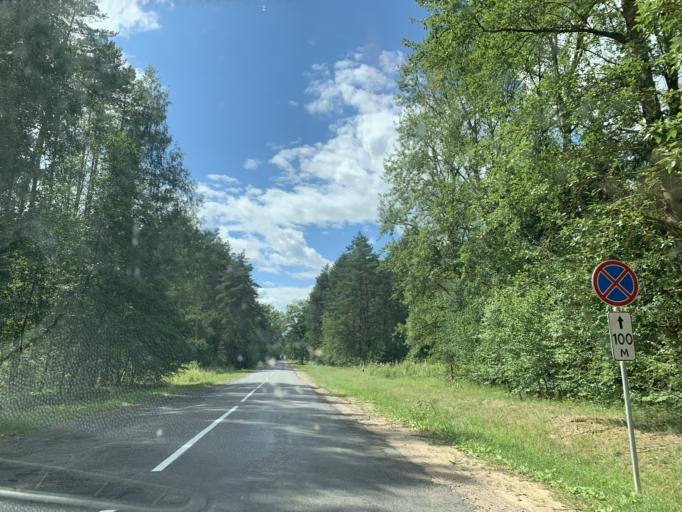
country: BY
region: Minsk
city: Rakaw
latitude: 53.9855
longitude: 26.9777
